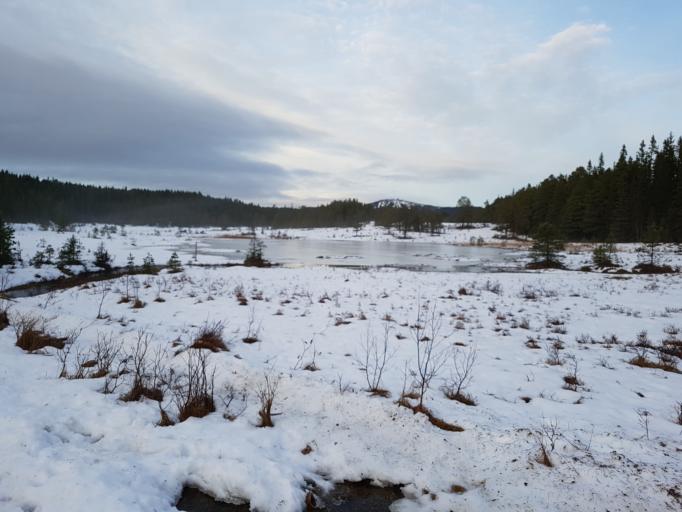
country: NO
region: Sor-Trondelag
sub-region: Melhus
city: Melhus
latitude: 63.3735
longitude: 10.2869
